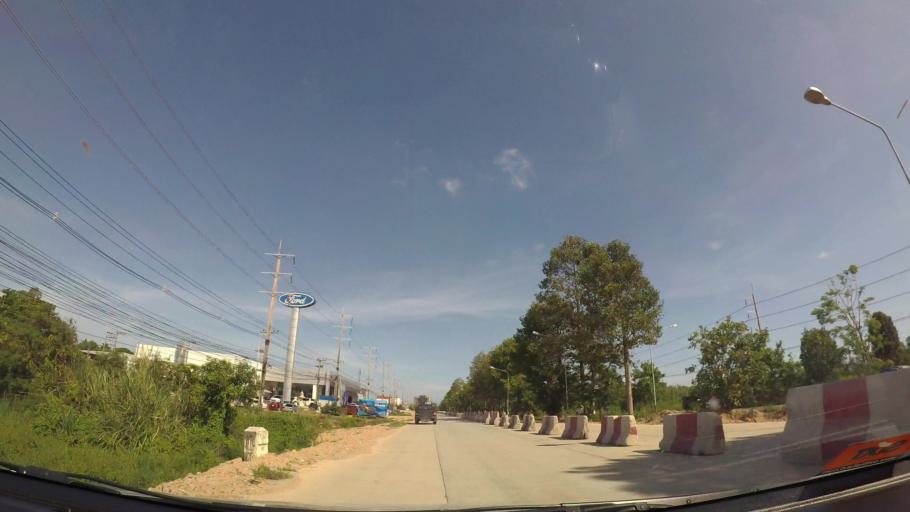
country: TH
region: Rayong
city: Rayong
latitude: 12.6703
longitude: 101.3062
